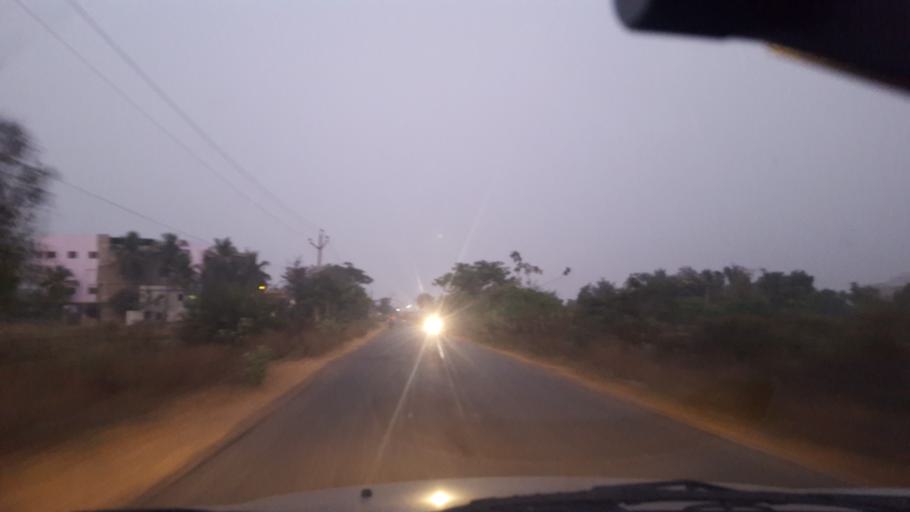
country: IN
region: Andhra Pradesh
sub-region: Srikakulam
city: Palasa
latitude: 18.7406
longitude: 84.4106
